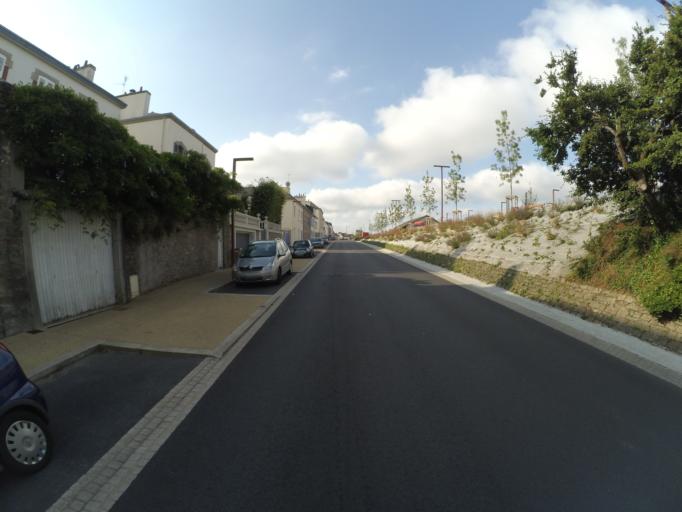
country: FR
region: Brittany
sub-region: Departement du Finistere
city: Quimperle
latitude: 47.8719
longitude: -3.5529
